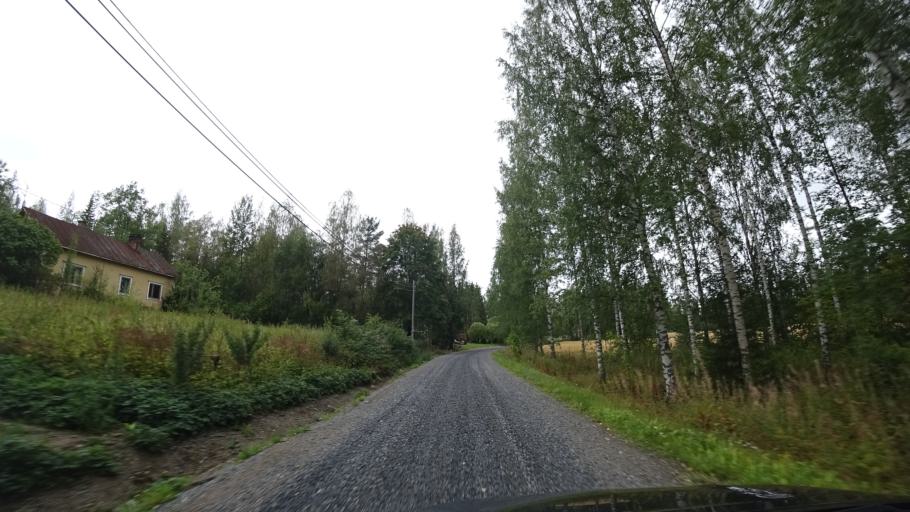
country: FI
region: Haeme
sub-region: Haemeenlinna
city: Lammi
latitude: 61.1251
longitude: 24.9838
